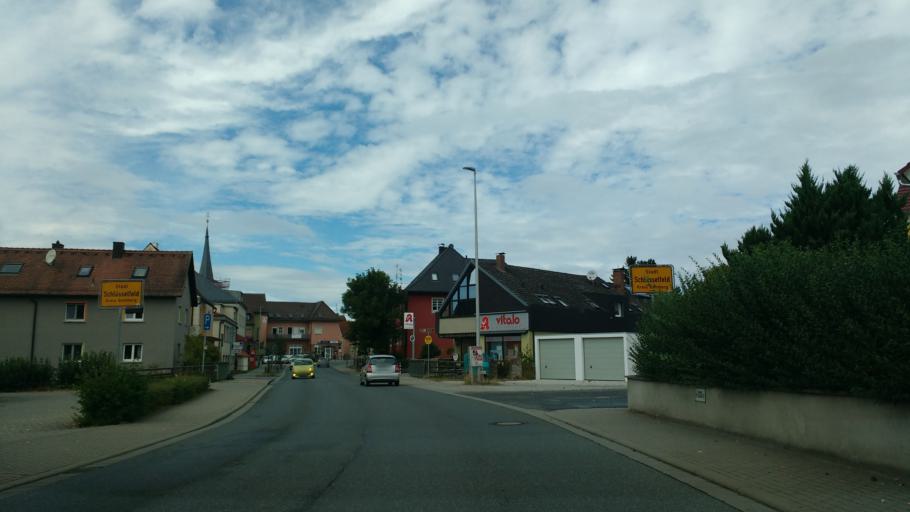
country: DE
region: Bavaria
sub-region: Upper Franconia
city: Schlusselfeld
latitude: 49.7560
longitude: 10.6225
